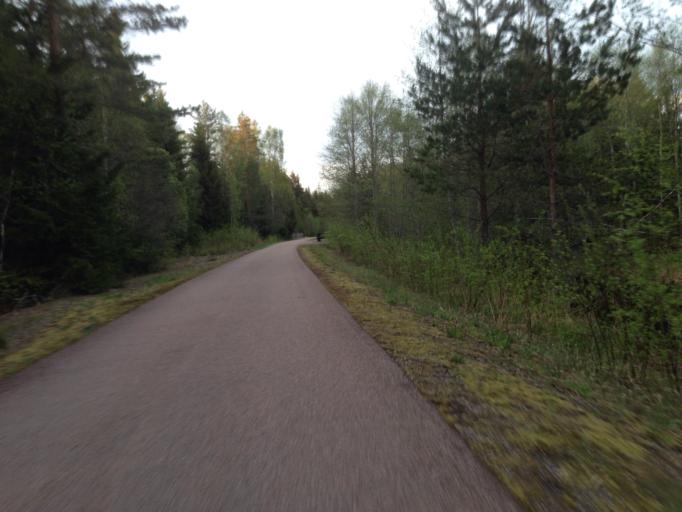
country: SE
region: Dalarna
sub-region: Ludvika Kommun
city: Grangesberg
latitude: 60.1341
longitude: 15.0714
